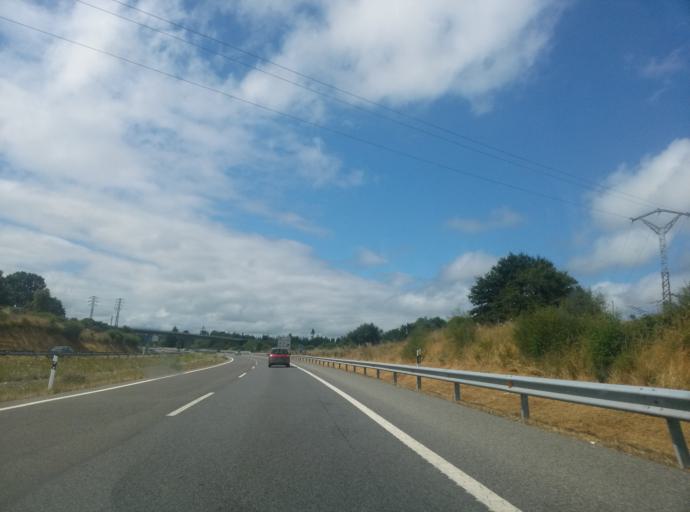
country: ES
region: Galicia
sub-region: Provincia de Lugo
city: Rabade
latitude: 43.1249
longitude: -7.6140
